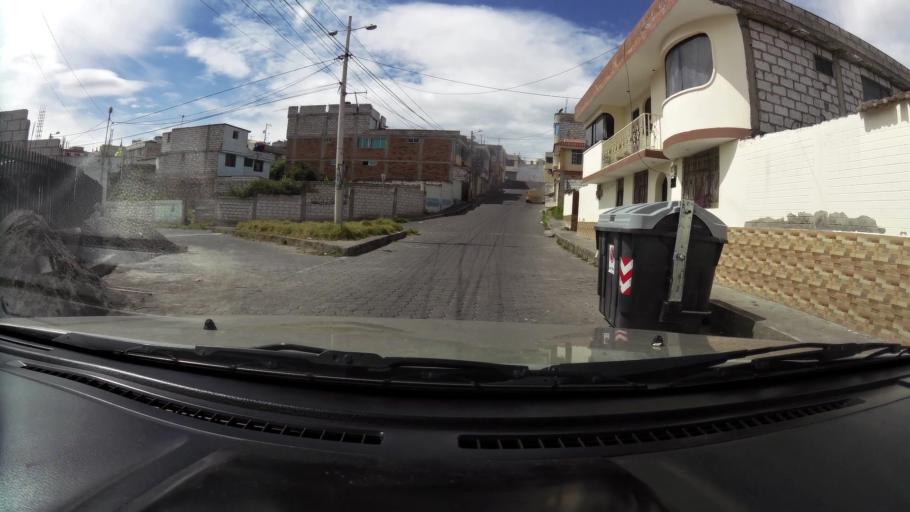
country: EC
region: Cotopaxi
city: Latacunga
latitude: -0.9343
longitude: -78.6041
